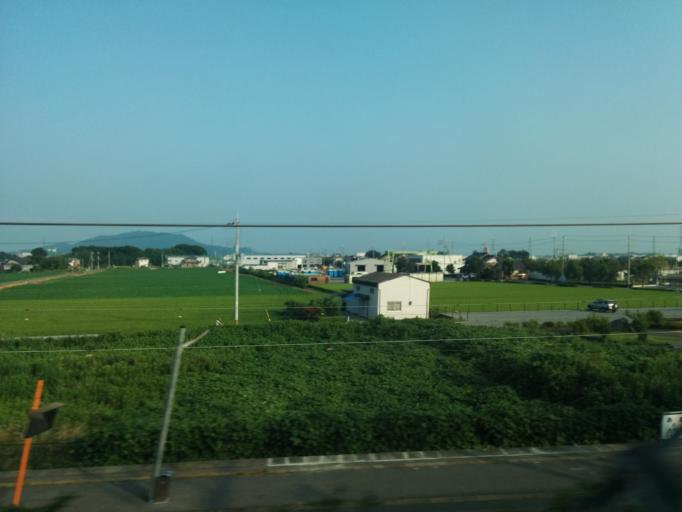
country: JP
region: Shiga Prefecture
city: Hikone
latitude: 35.2133
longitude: 136.2461
